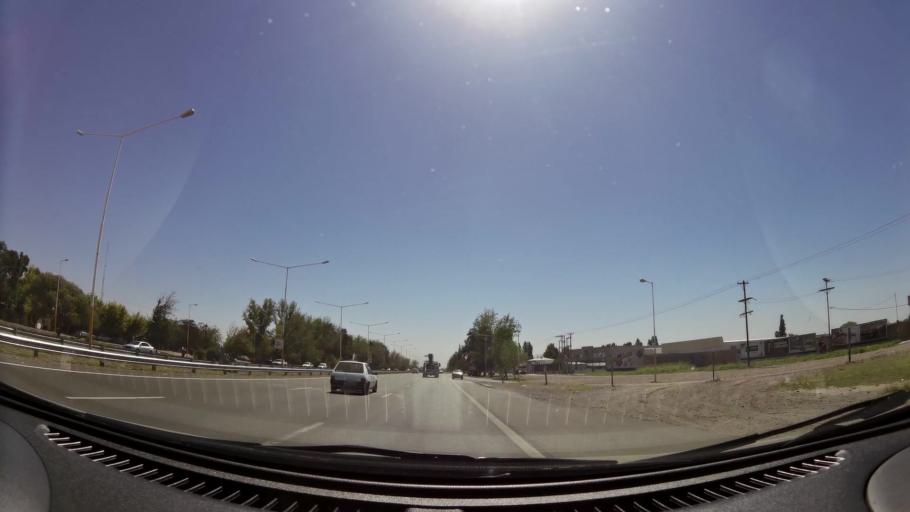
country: AR
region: Mendoza
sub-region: Departamento de Godoy Cruz
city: Godoy Cruz
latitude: -32.9663
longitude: -68.8410
